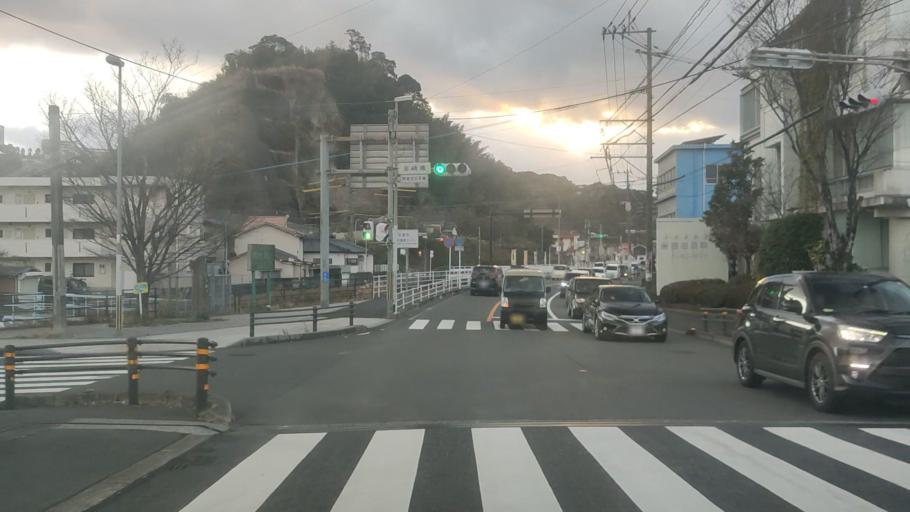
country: JP
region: Kagoshima
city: Kagoshima-shi
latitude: 31.6133
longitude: 130.5286
